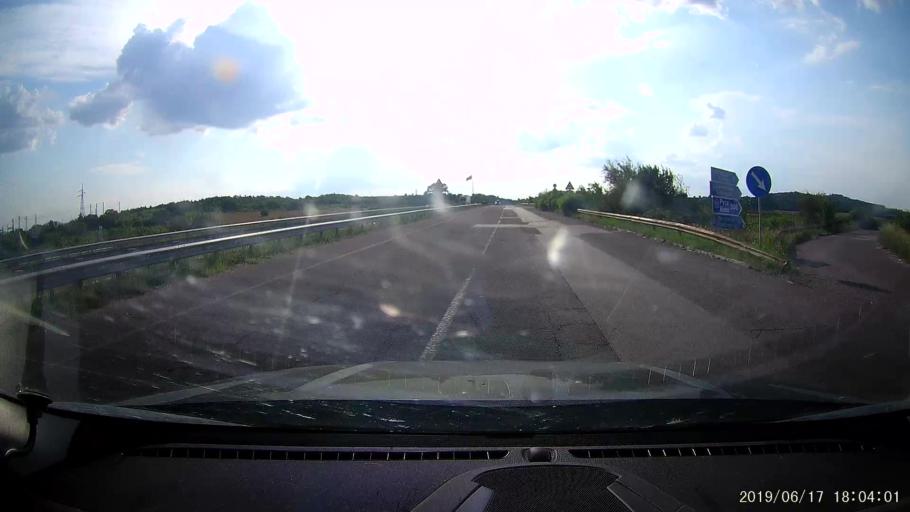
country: BG
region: Khaskovo
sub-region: Obshtina Svilengrad
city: Svilengrad
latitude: 41.7825
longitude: 26.2079
